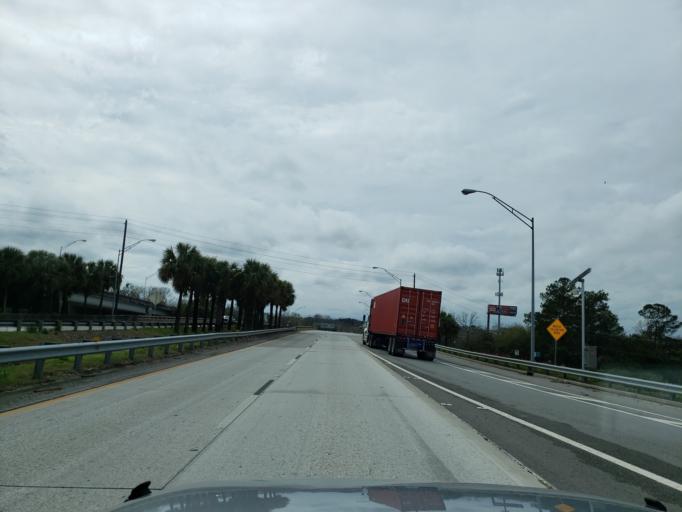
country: US
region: Georgia
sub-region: Chatham County
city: Savannah
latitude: 32.0709
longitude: -81.1063
